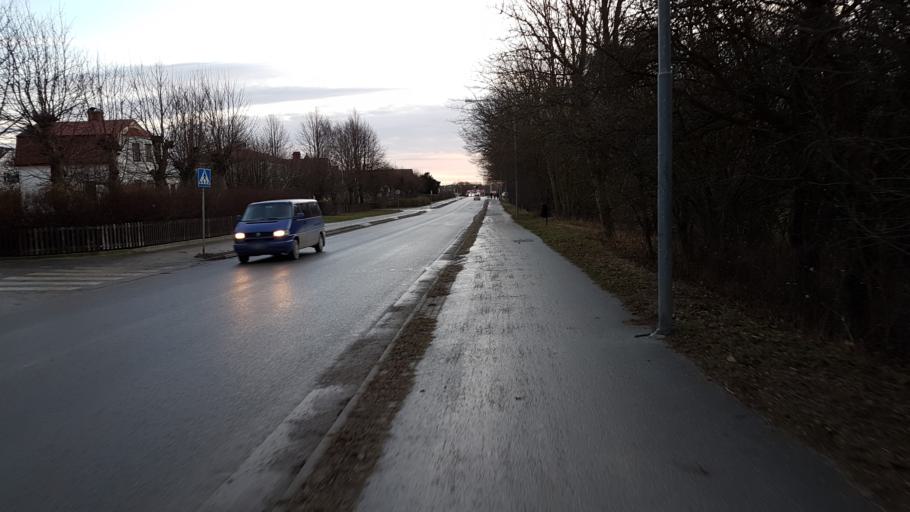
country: SE
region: Gotland
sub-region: Gotland
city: Visby
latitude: 57.6199
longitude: 18.2841
